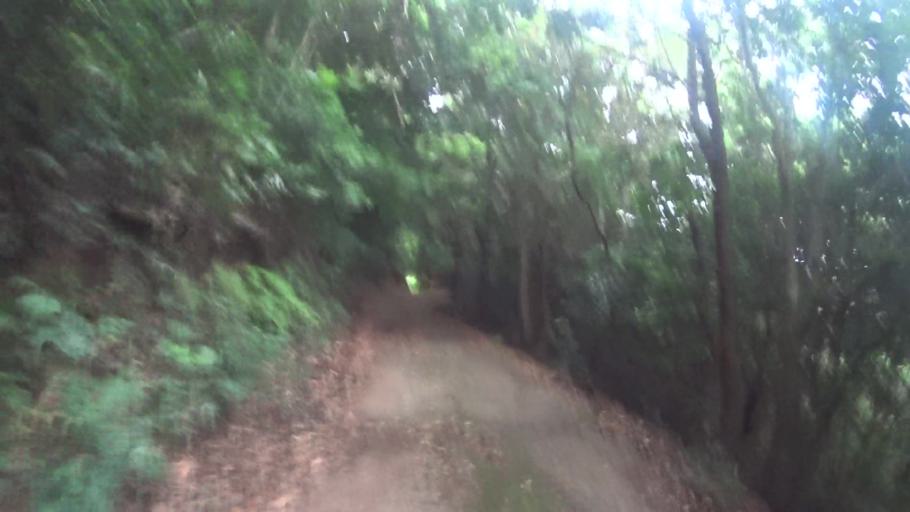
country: JP
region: Nagasaki
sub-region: Hirado Shi
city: Hirado
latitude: 33.1860
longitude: 129.3595
